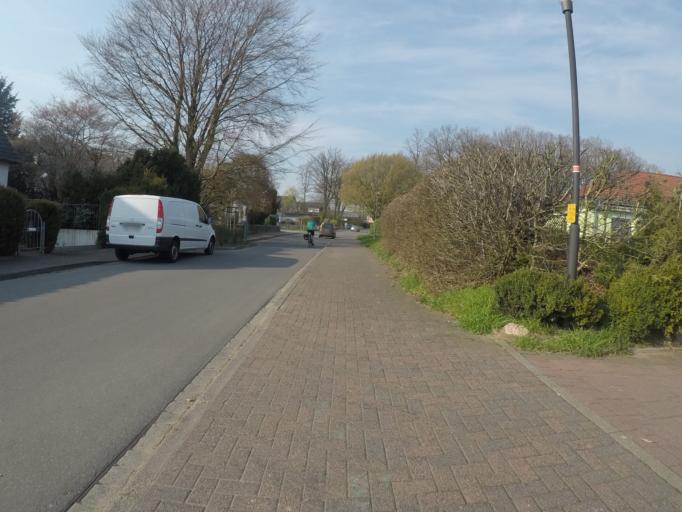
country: DE
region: Schleswig-Holstein
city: Wittenborn
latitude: 53.9207
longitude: 10.2213
